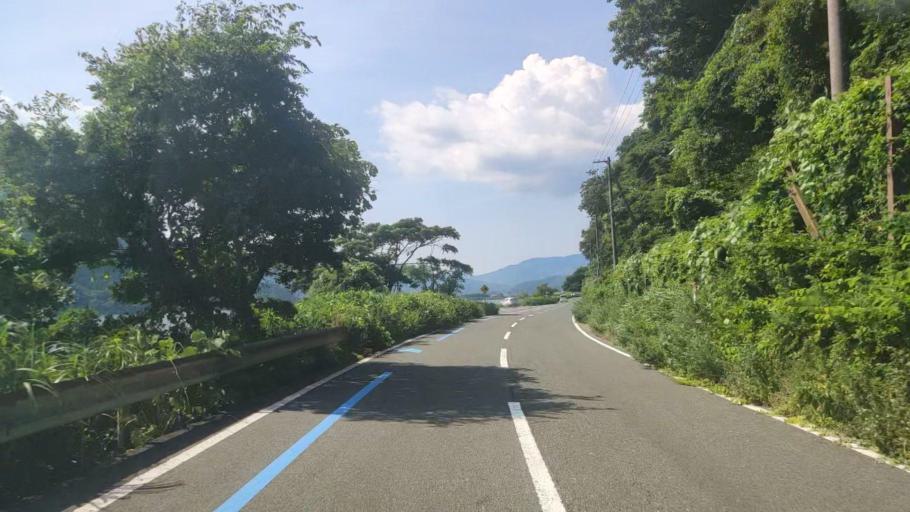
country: JP
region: Shiga Prefecture
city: Nagahama
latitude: 35.5027
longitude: 136.1701
